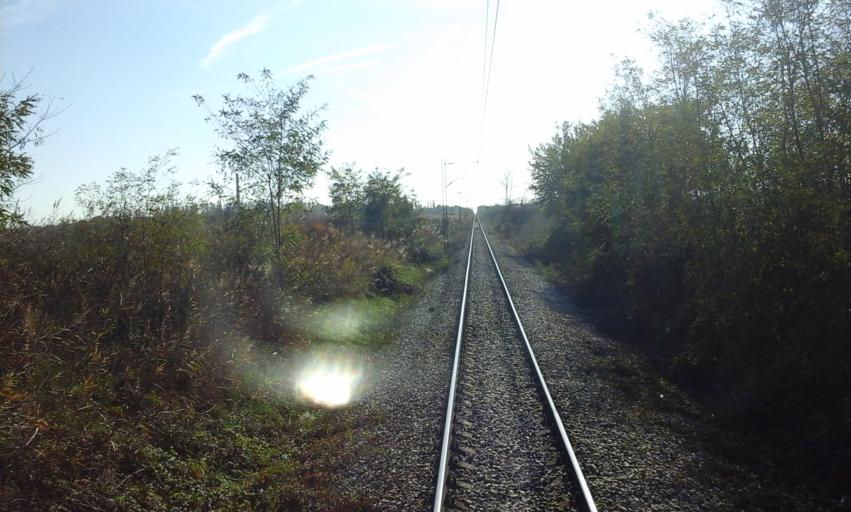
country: RS
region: Autonomna Pokrajina Vojvodina
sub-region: Severnobacki Okrug
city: Subotica
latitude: 46.0771
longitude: 19.6895
